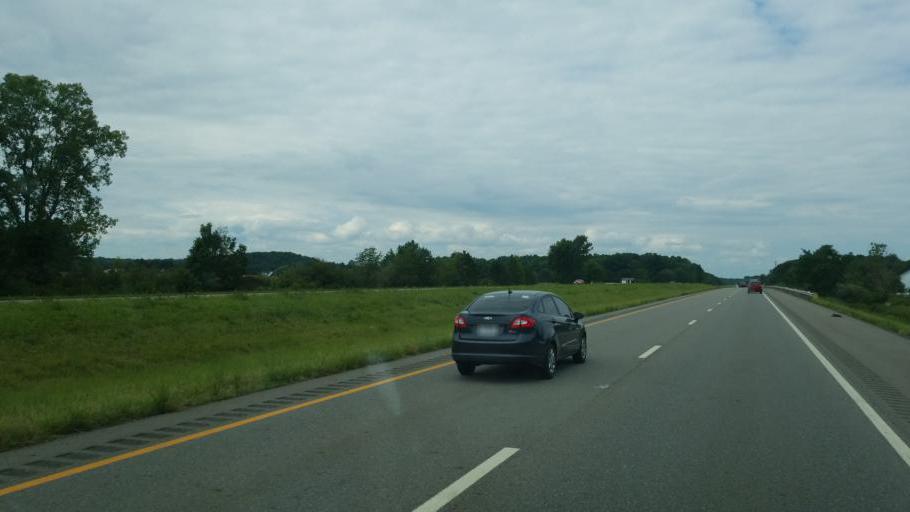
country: US
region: Ohio
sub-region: Mahoning County
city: Canfield
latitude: 40.9699
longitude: -80.7199
